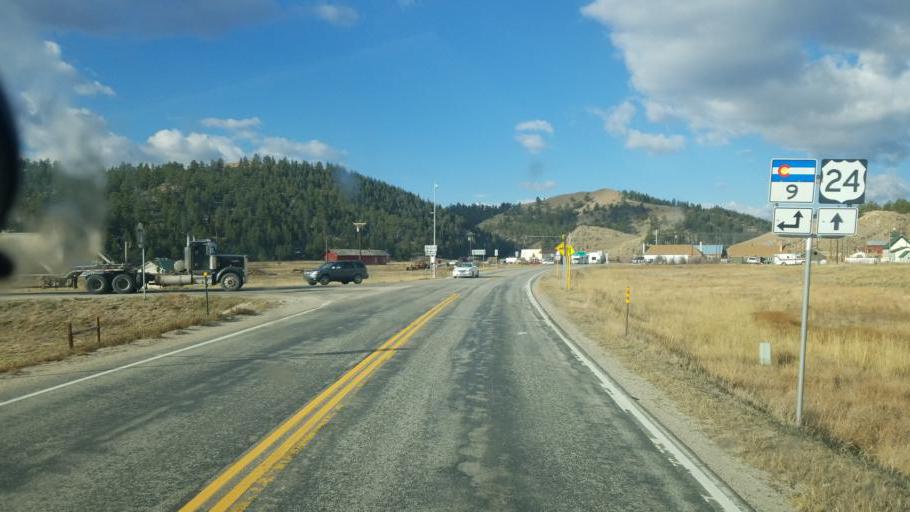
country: US
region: Colorado
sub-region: Park County
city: Fairplay
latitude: 39.0217
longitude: -105.7933
